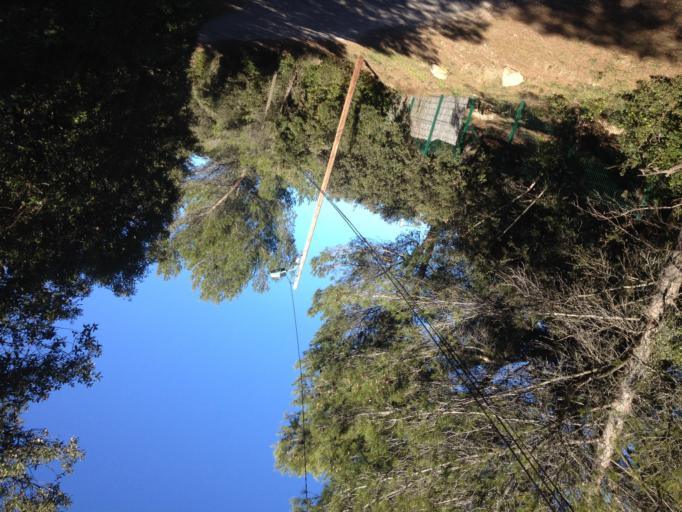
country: FR
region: Provence-Alpes-Cote d'Azur
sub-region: Departement du Vaucluse
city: Orange
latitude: 44.1251
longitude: 4.8052
